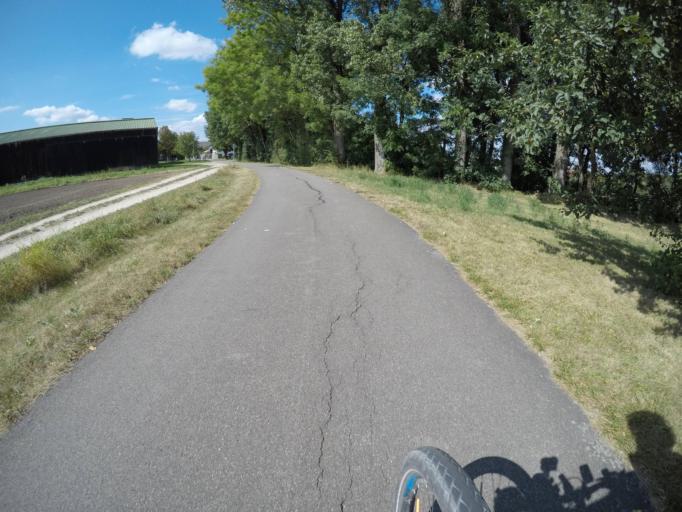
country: DE
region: Bavaria
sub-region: Swabia
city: Dillingen an der Donau
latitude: 48.6039
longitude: 10.4593
